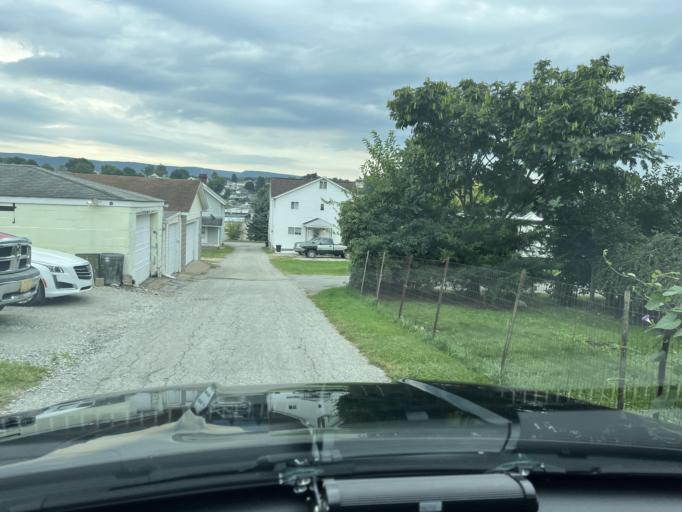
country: US
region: Pennsylvania
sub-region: Fayette County
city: South Uniontown
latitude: 39.8967
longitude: -79.7397
